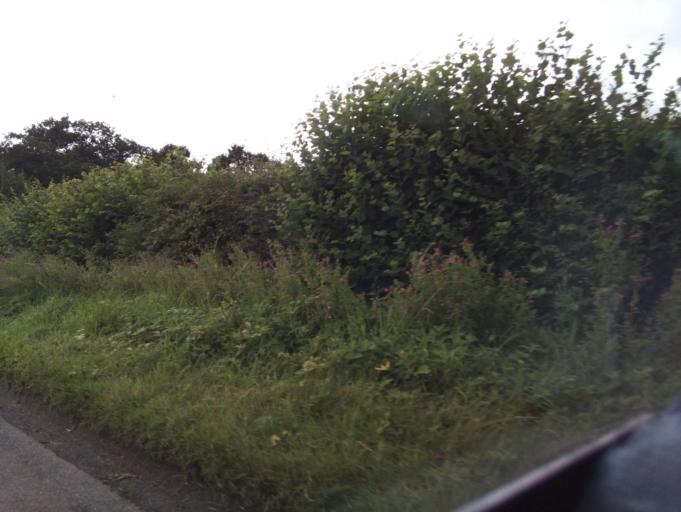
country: GB
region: England
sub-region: Solihull
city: Dickens Heath
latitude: 52.3766
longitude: -1.8289
